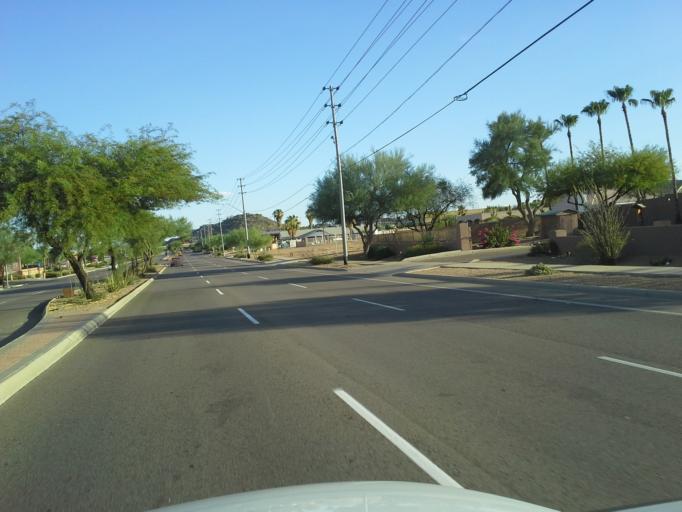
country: US
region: Arizona
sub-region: Maricopa County
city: Cave Creek
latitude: 33.6802
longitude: -112.0312
